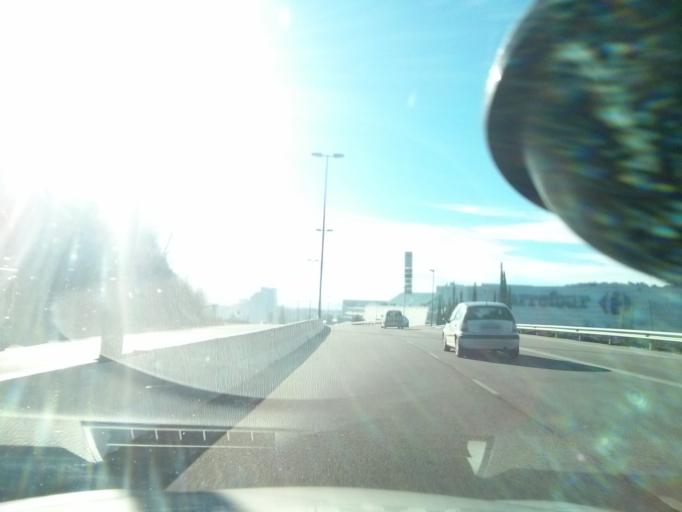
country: ES
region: Castille and Leon
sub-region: Provincia de Burgos
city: Burgos
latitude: 42.3617
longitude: -3.6944
